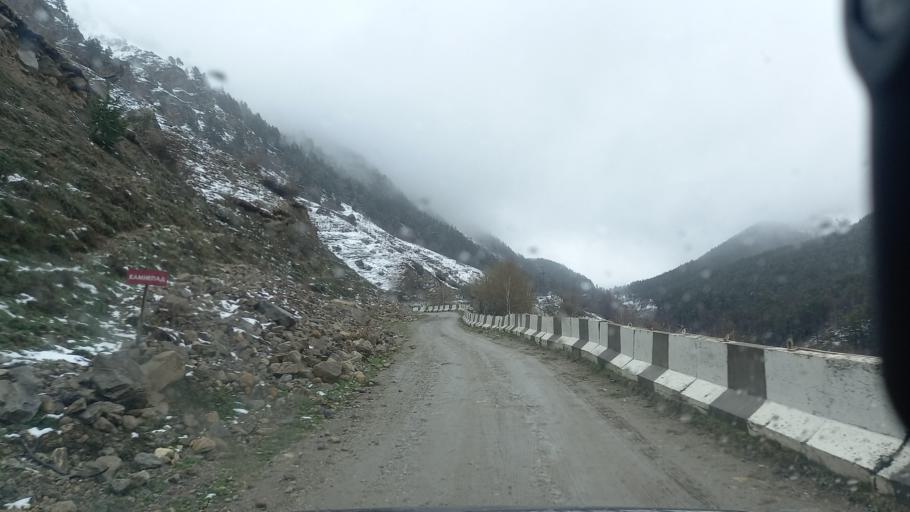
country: RU
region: Kabardino-Balkariya
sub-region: El'brusskiy Rayon
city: El'brus
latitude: 43.2255
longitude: 42.6722
